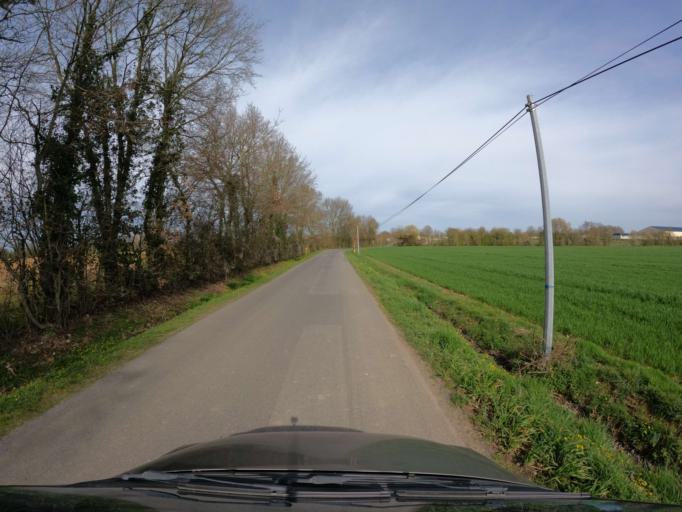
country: FR
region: Pays de la Loire
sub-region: Departement de la Vendee
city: Bouffere
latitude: 46.9529
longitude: -1.3683
